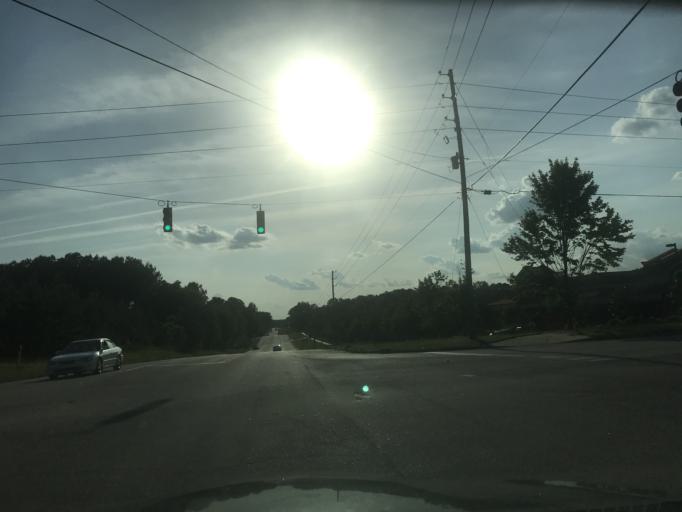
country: US
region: North Carolina
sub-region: Wake County
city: Knightdale
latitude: 35.7544
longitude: -78.5168
